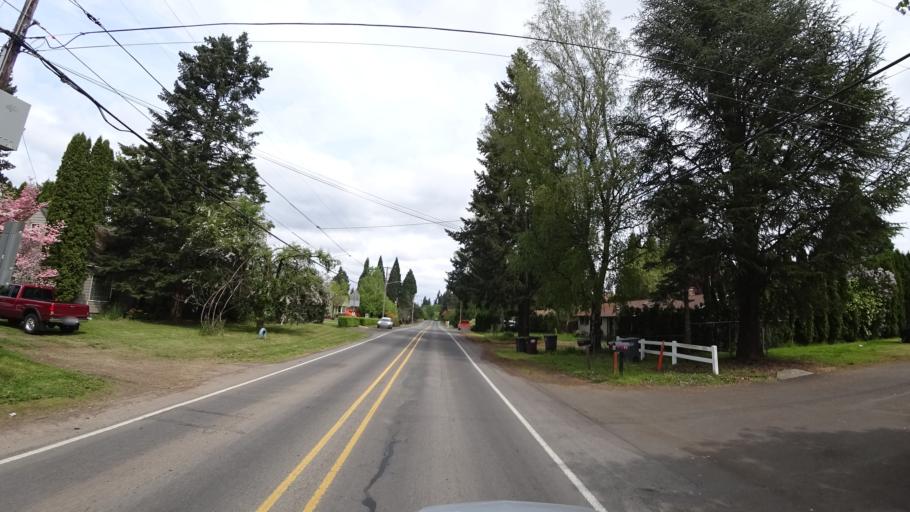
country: US
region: Oregon
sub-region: Washington County
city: Hillsboro
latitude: 45.5319
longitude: -122.9937
